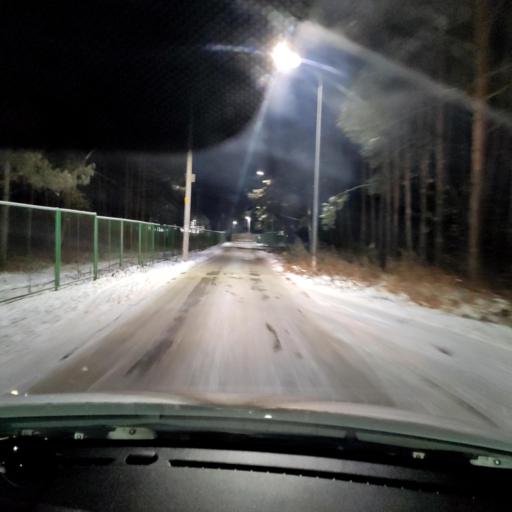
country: RU
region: Tatarstan
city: Verkhniy Uslon
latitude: 55.6232
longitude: 49.0195
